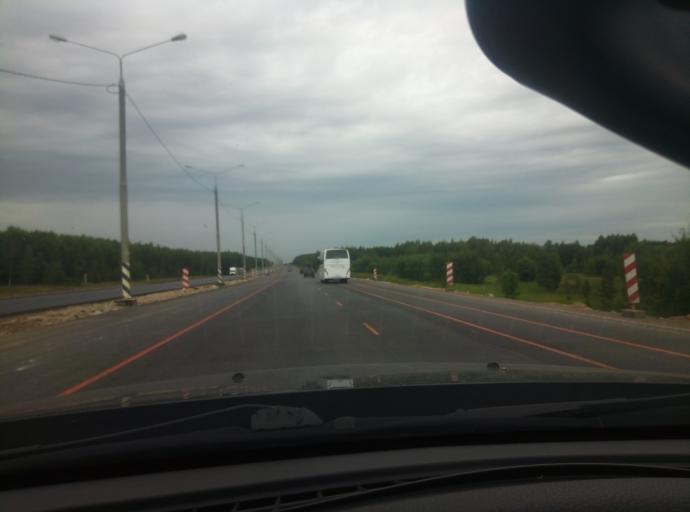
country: RU
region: Tula
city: Yasnogorsk
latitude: 54.5376
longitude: 37.5181
